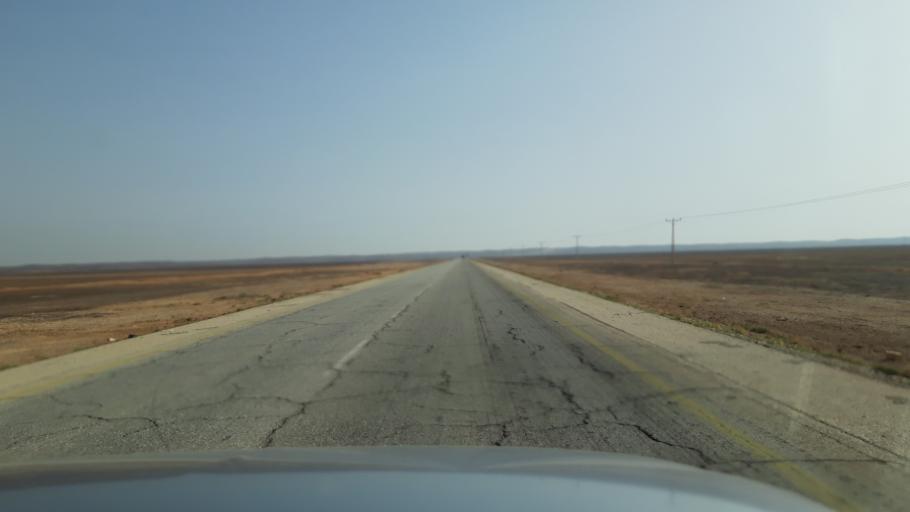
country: JO
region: Amman
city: Al Azraq ash Shamali
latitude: 31.8331
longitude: 36.6286
